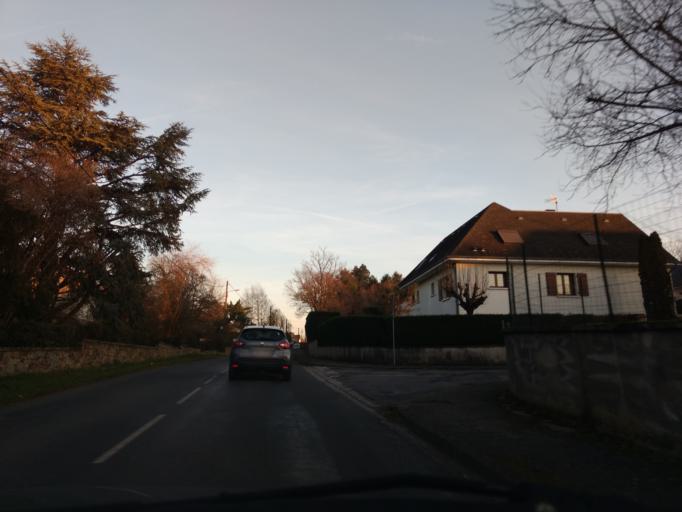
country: FR
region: Midi-Pyrenees
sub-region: Departement de l'Aveyron
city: Naucelle
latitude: 44.1953
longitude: 2.3489
